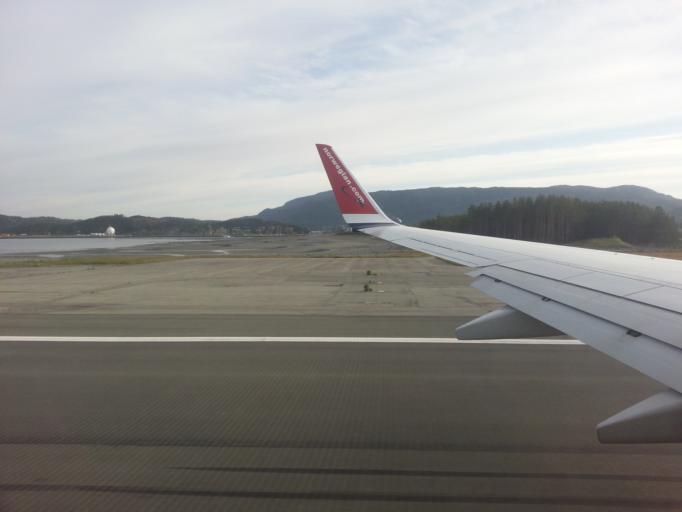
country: NO
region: Nord-Trondelag
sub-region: Stjordal
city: Stjordal
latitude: 63.4577
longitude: 10.9014
